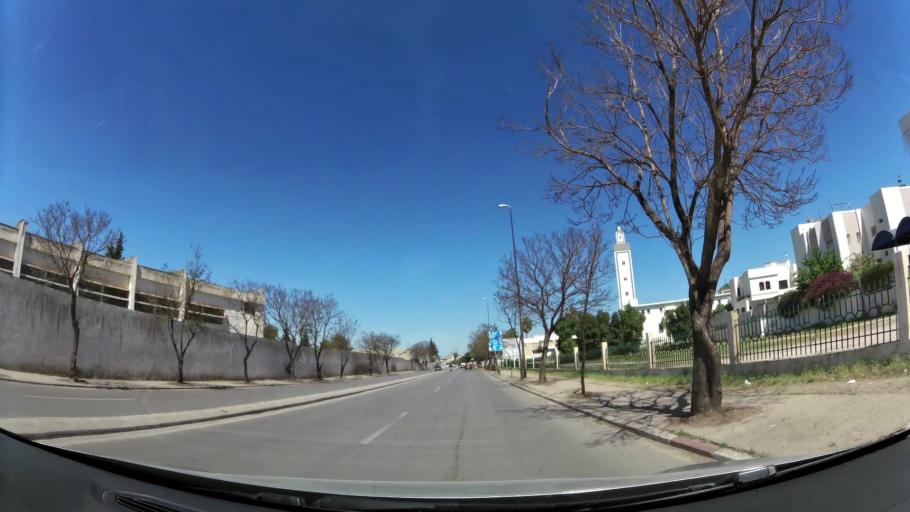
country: MA
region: Fes-Boulemane
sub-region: Fes
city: Fes
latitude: 34.0148
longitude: -4.9987
